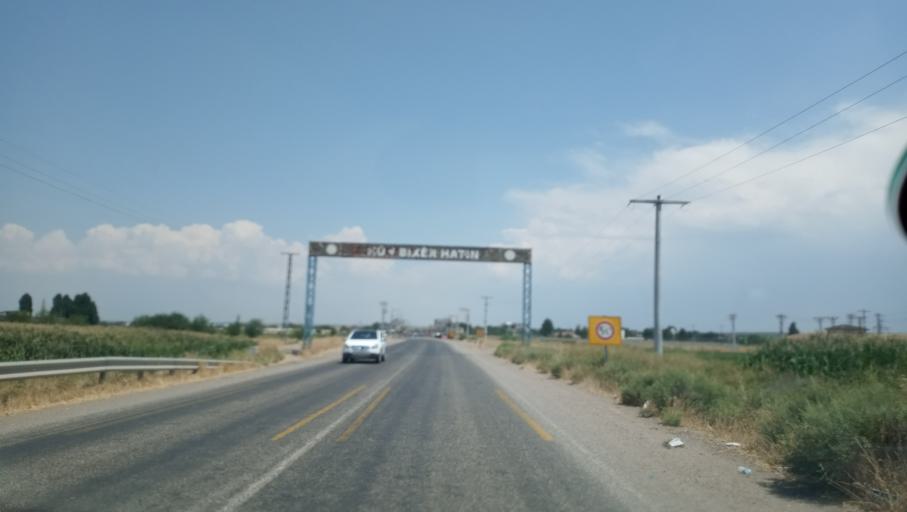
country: TR
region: Diyarbakir
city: Tepe
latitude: 37.7934
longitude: 40.7563
